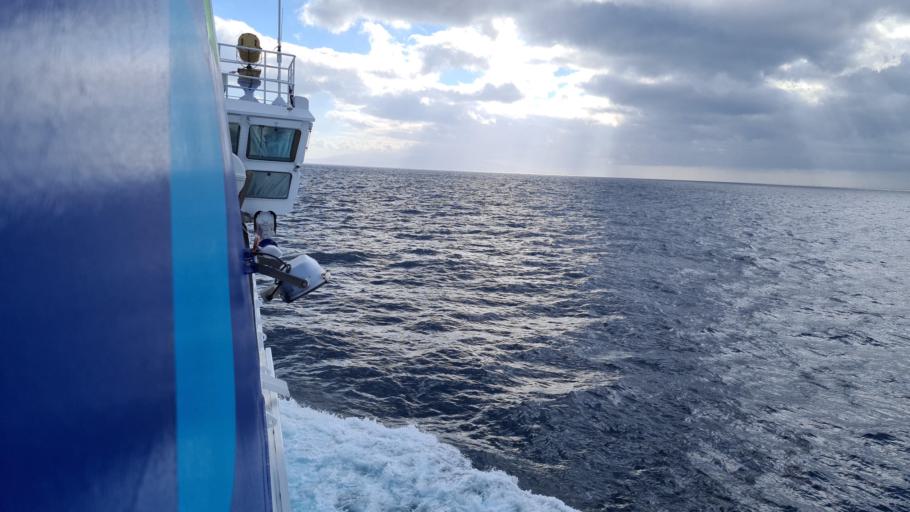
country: PT
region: Azores
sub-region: Sao Roque do Pico
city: Sao Roque do Pico
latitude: 38.6305
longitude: -28.3279
